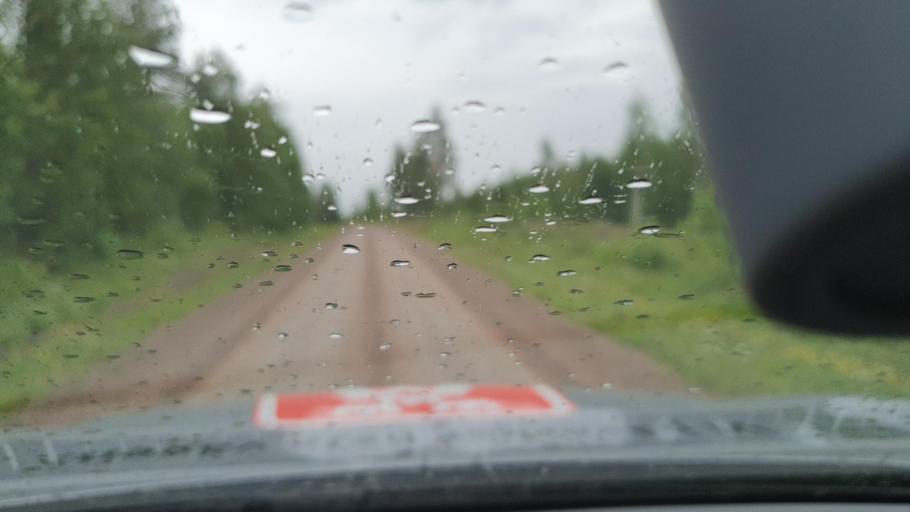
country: SE
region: Norrbotten
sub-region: Overkalix Kommun
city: OEverkalix
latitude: 66.5107
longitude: 22.7487
